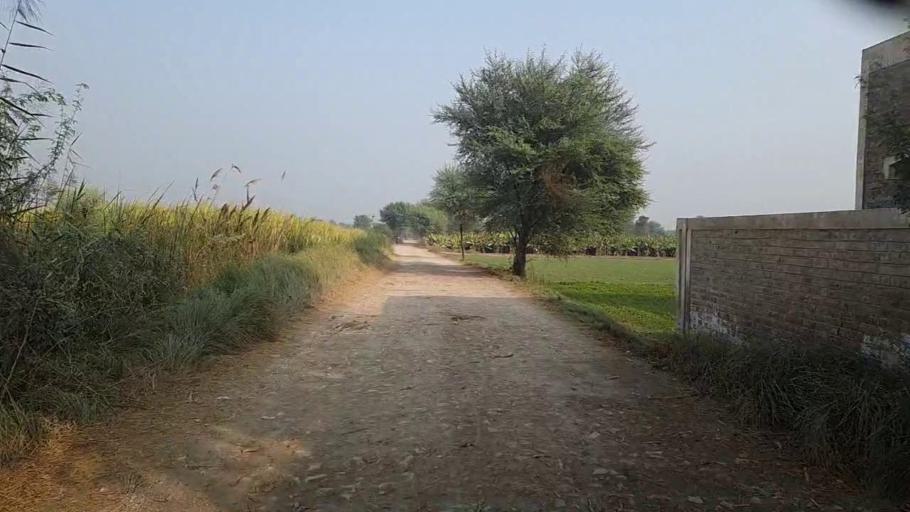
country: PK
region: Sindh
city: Kandiari
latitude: 27.0087
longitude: 68.4842
